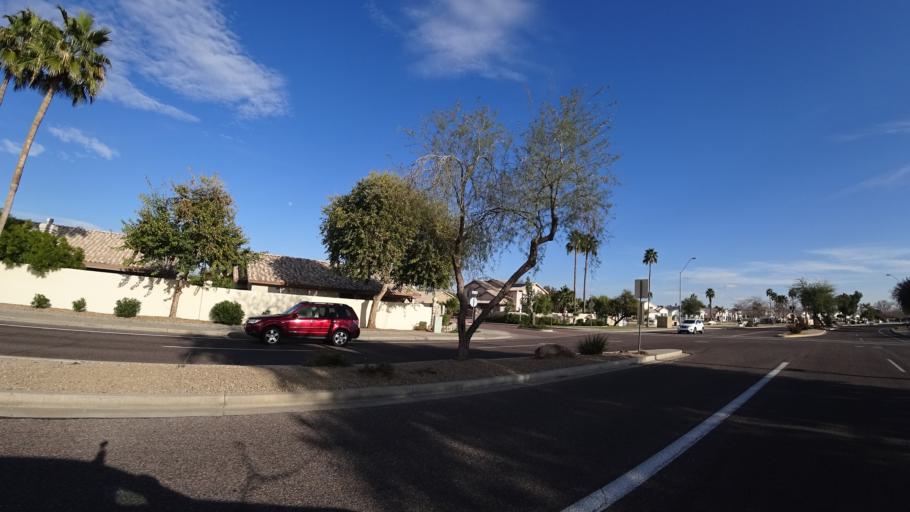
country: US
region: Arizona
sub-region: Maricopa County
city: Sun City
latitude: 33.6179
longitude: -112.2542
